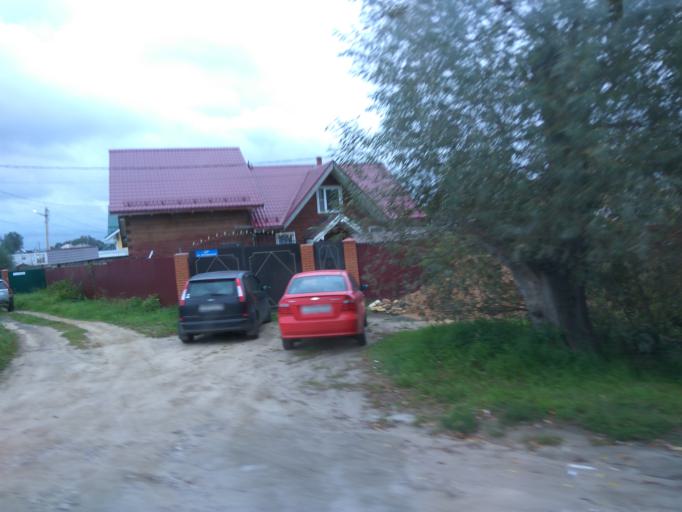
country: RU
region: Moskovskaya
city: Malyshevo
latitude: 55.5353
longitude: 38.3272
